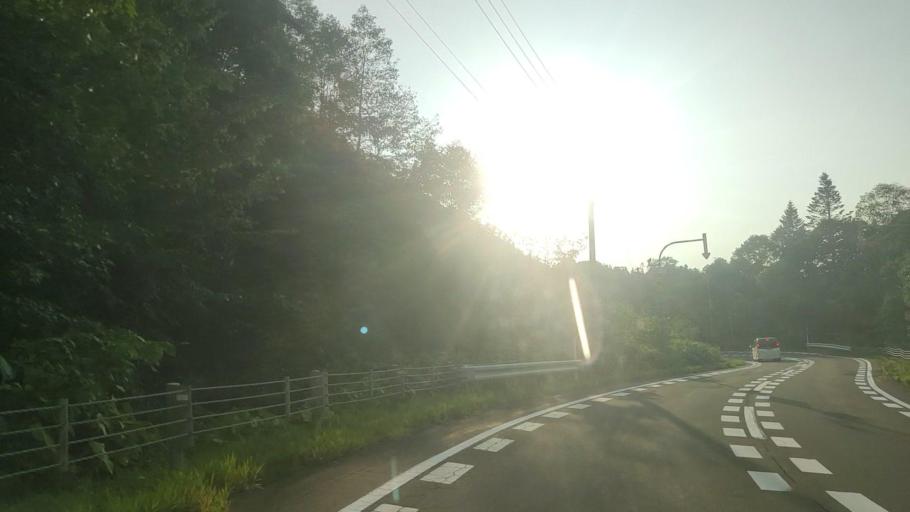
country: JP
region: Hokkaido
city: Bibai
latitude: 43.1687
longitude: 142.0759
